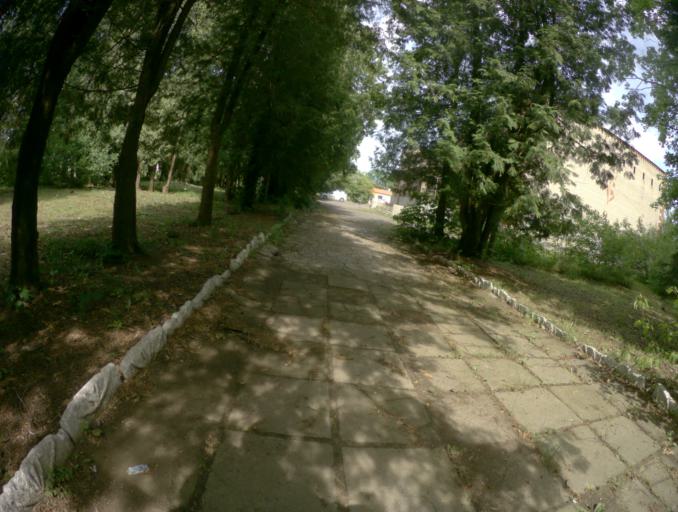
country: RU
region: Vladimir
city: Stavrovo
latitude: 56.0923
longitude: 39.9729
